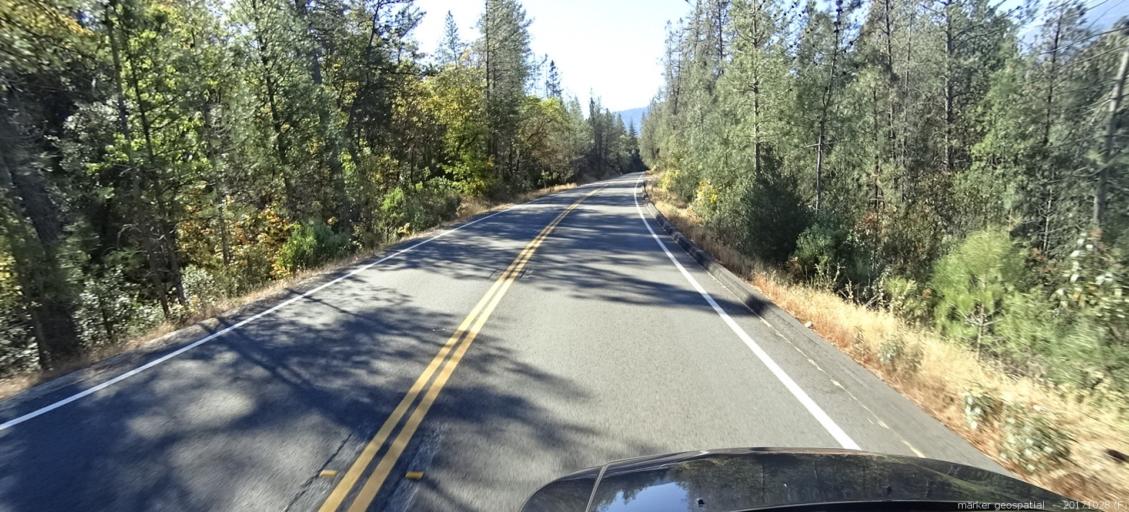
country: US
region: California
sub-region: Shasta County
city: Shasta
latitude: 40.6053
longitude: -122.5302
